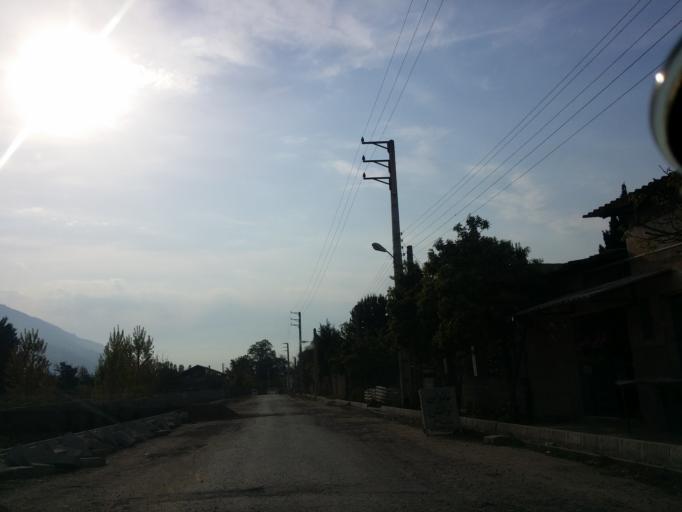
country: IR
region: Mazandaran
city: Chalus
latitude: 36.6573
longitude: 51.3937
